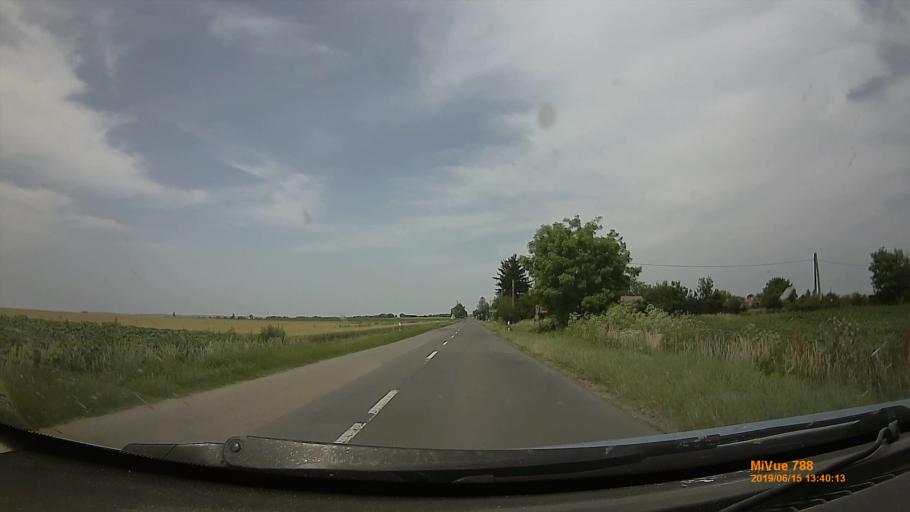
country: HU
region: Tolna
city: Iregszemcse
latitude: 46.6400
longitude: 18.1974
